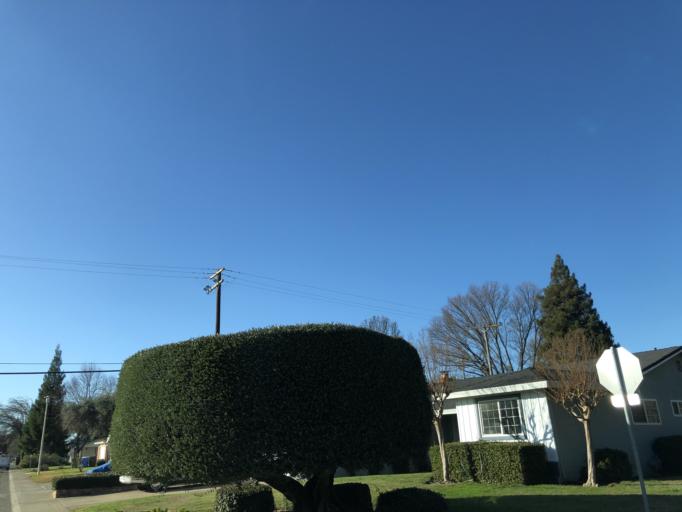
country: US
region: California
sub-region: Sacramento County
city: Rosemont
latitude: 38.5528
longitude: -121.4000
